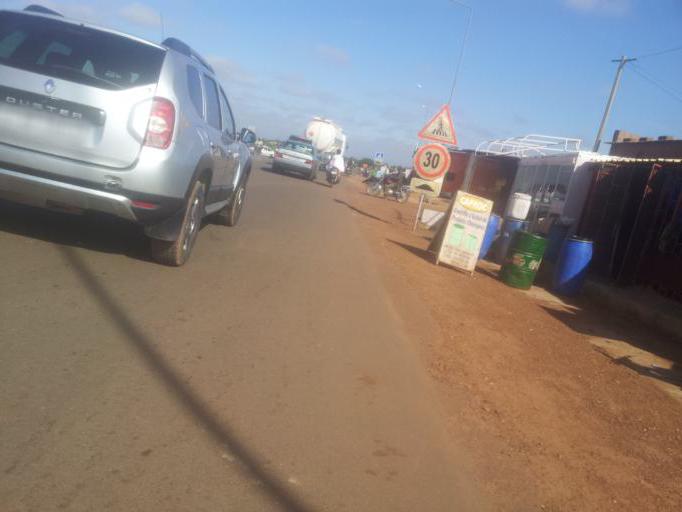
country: BF
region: Centre
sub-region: Kadiogo Province
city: Ouagadougou
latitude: 12.3699
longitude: -1.5653
